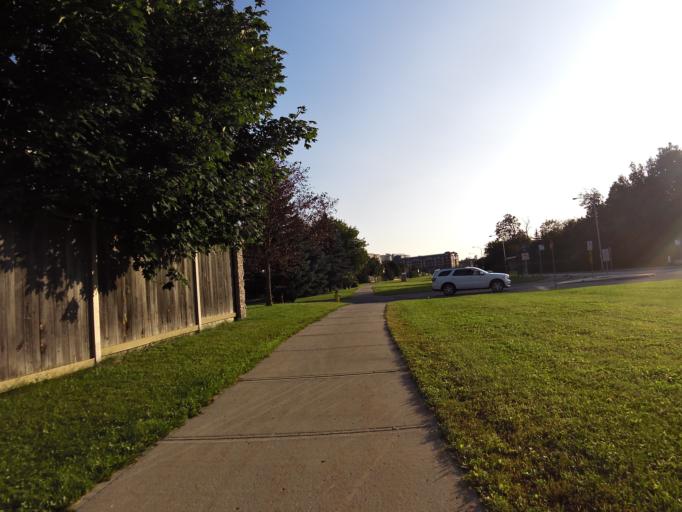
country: CA
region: Ontario
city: Bells Corners
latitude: 45.3191
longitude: -75.8962
